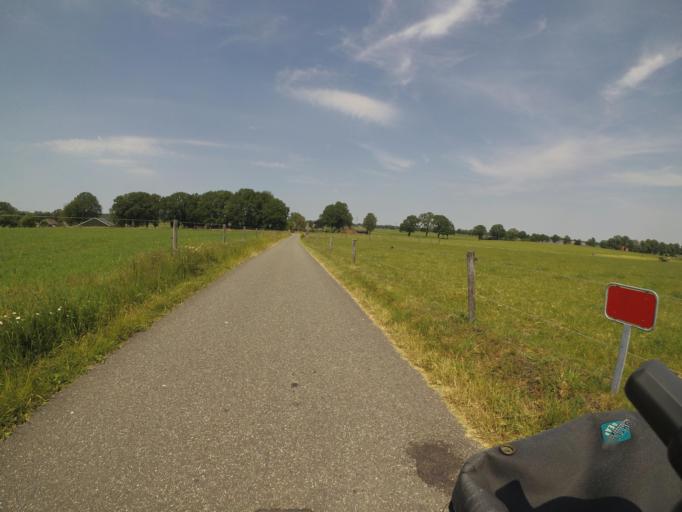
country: NL
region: Overijssel
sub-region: Gemeente Hof van Twente
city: Markelo
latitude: 52.2814
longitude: 6.4661
